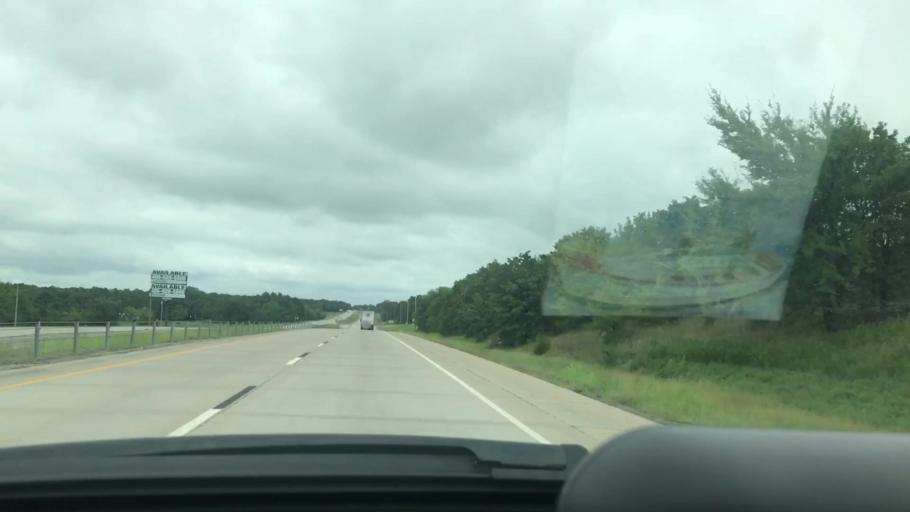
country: US
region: Oklahoma
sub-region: Pittsburg County
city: McAlester
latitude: 34.7000
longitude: -95.9078
